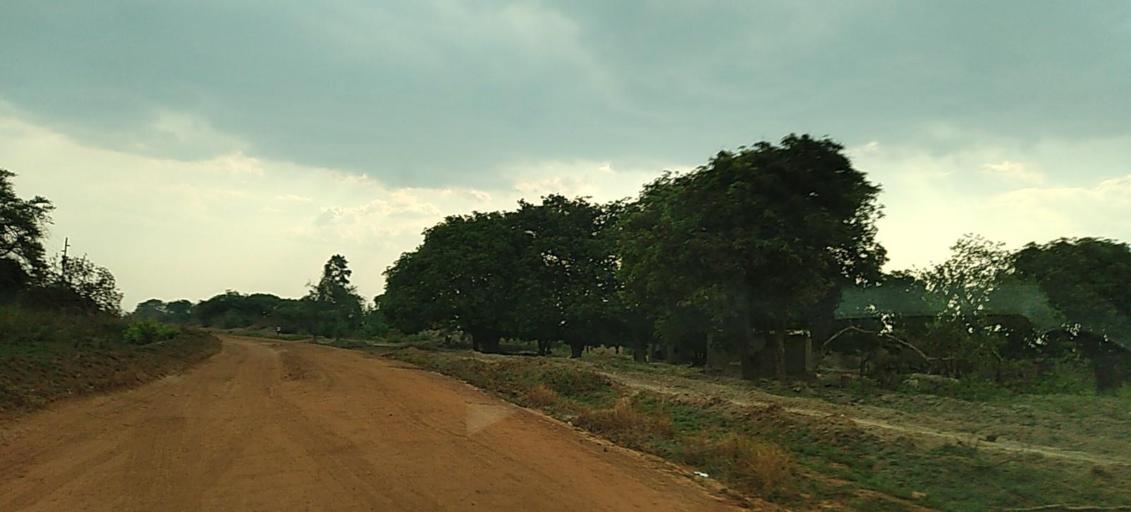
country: ZM
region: Copperbelt
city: Kalulushi
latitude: -12.9383
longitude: 27.9261
